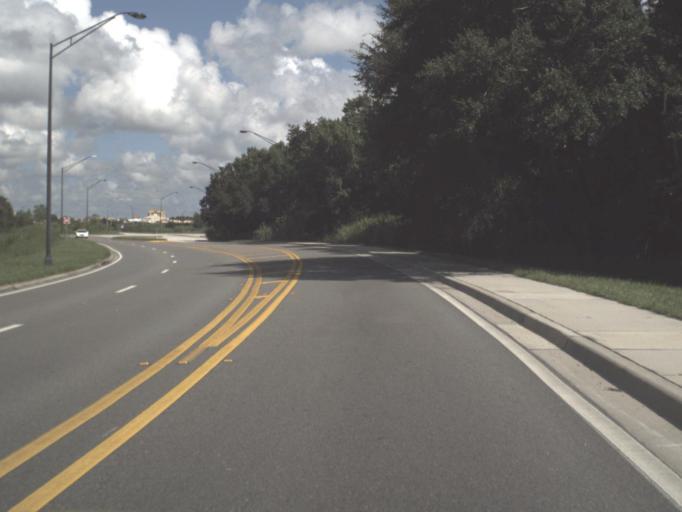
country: US
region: Florida
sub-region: Polk County
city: Medulla
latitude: 27.9909
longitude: -81.9753
